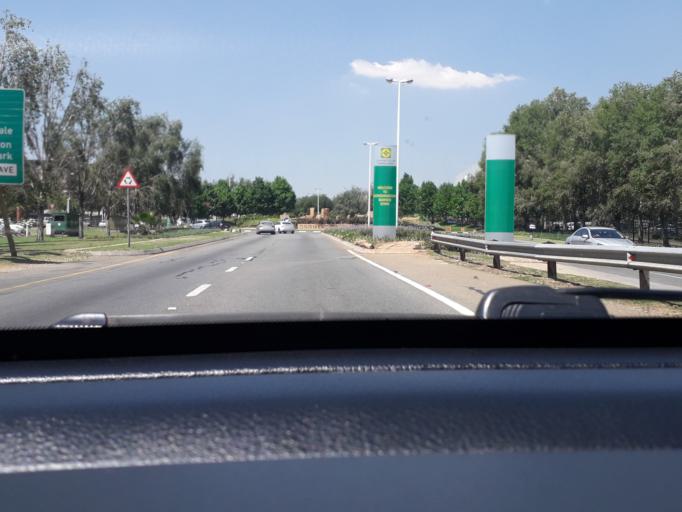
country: ZA
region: Gauteng
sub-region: City of Johannesburg Metropolitan Municipality
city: Modderfontein
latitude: -26.1161
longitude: 28.1351
